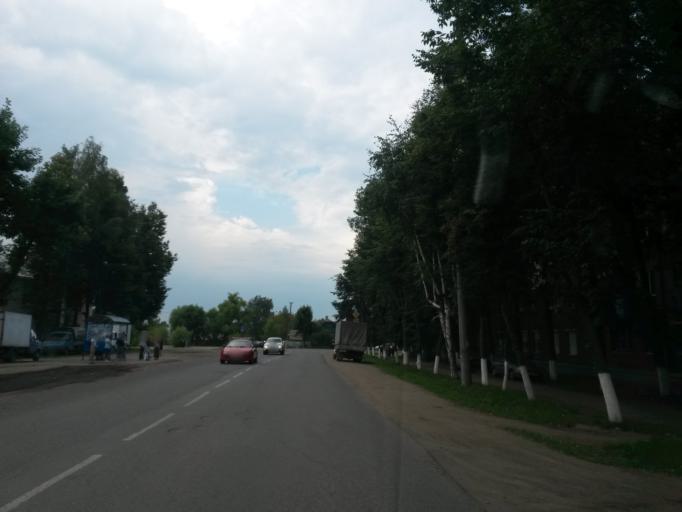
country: RU
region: Jaroslavl
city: Yaroslavl
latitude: 57.6070
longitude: 39.8141
